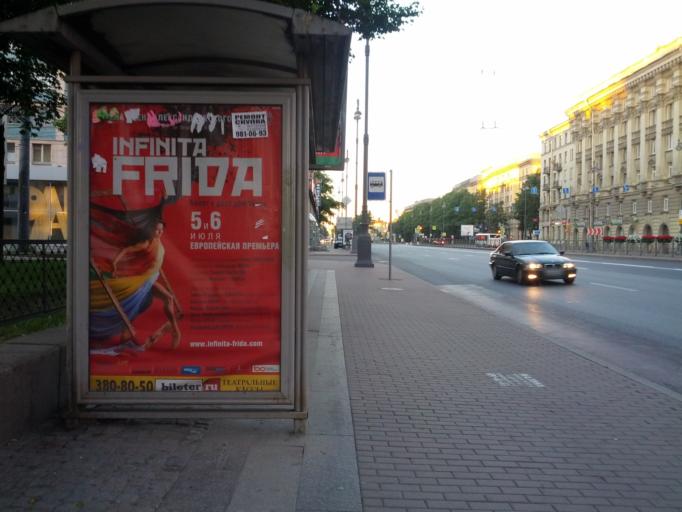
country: RU
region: St.-Petersburg
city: Admiralteisky
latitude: 59.9041
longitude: 30.3187
